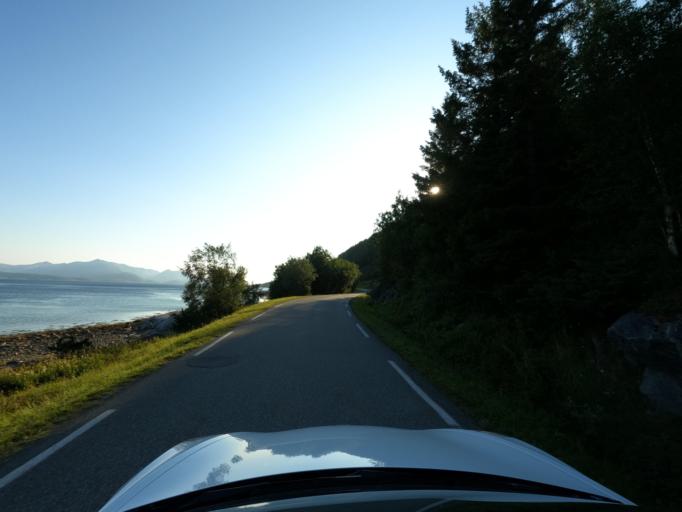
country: NO
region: Nordland
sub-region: Ballangen
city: Ballangen
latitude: 68.4613
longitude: 16.7606
